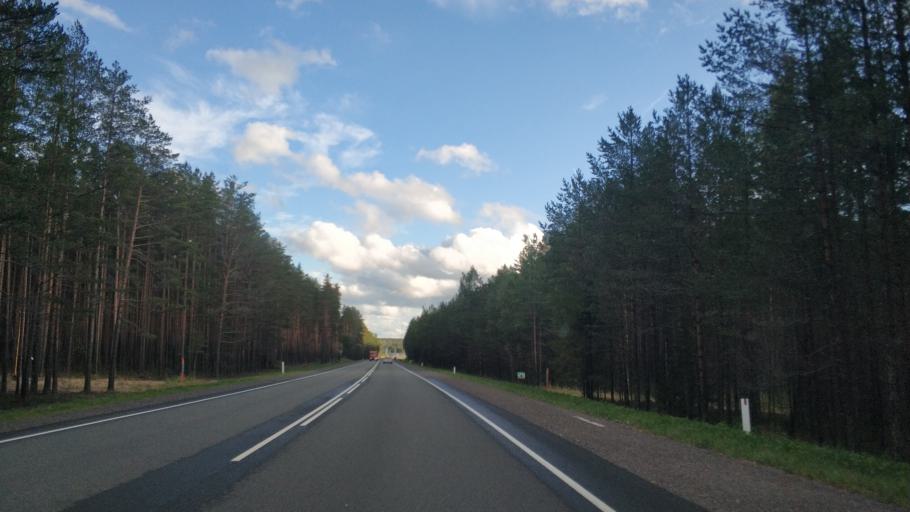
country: RU
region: Leningrad
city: Priozersk
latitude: 60.9844
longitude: 30.1837
